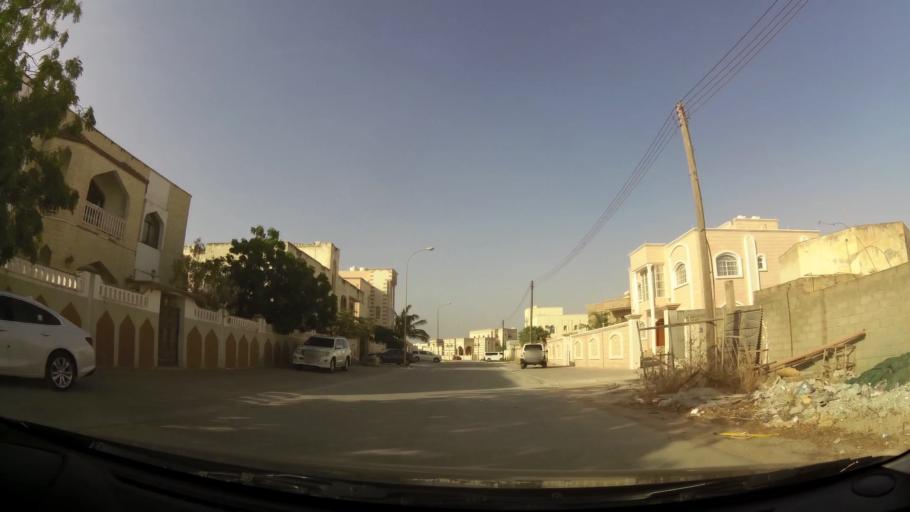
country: OM
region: Zufar
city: Salalah
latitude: 17.0184
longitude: 54.0208
